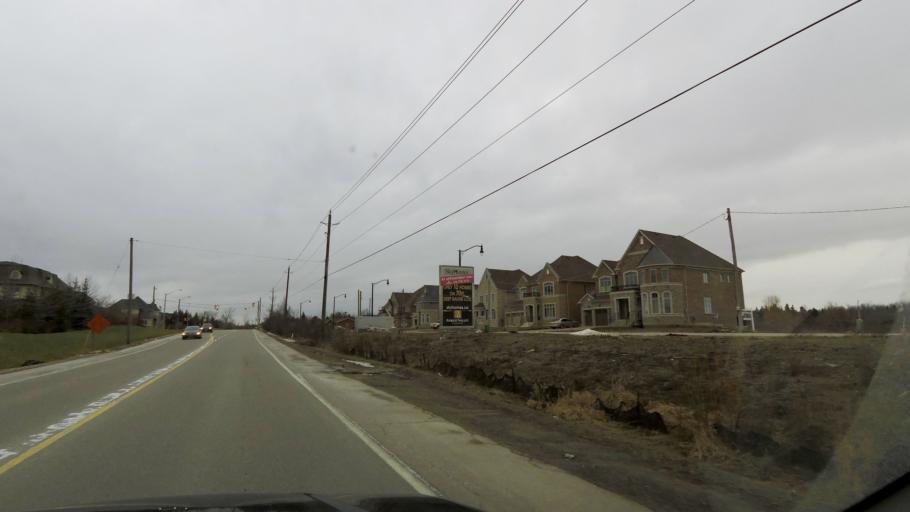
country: CA
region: Ontario
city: Brampton
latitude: 43.7950
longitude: -79.7411
